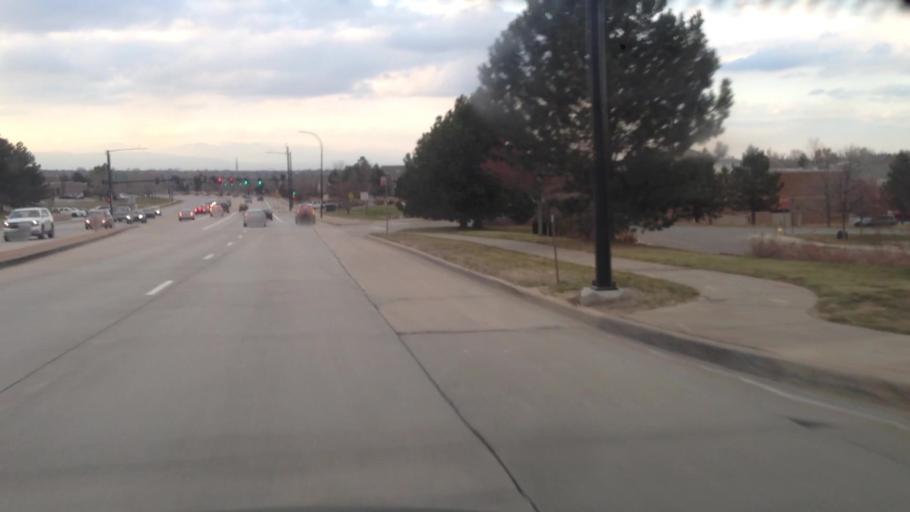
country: US
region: Colorado
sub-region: Douglas County
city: Carriage Club
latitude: 39.5408
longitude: -104.9116
